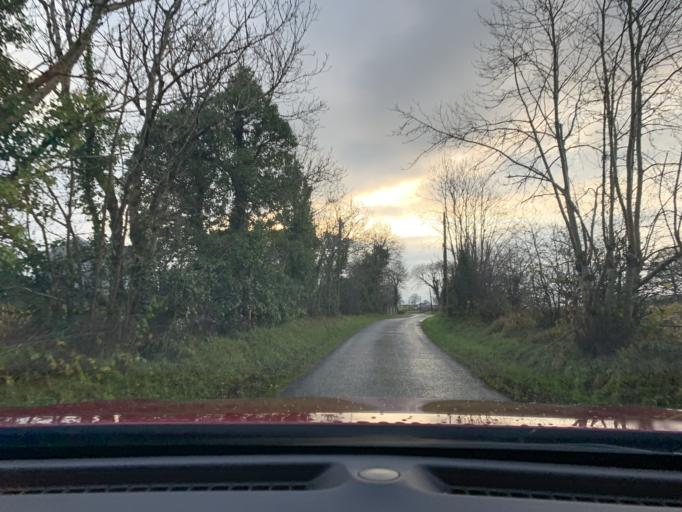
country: IE
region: Connaught
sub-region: Sligo
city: Ballymote
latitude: 54.0394
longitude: -8.5499
